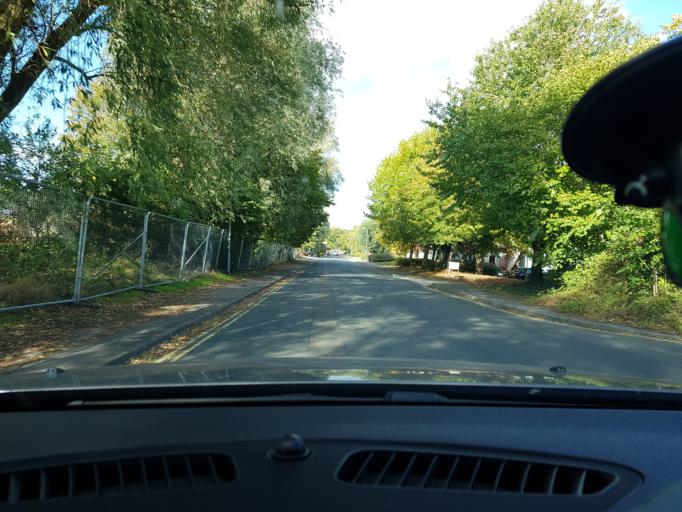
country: GB
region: England
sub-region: Borough of Swindon
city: Wanborough
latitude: 51.5564
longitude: -1.7239
